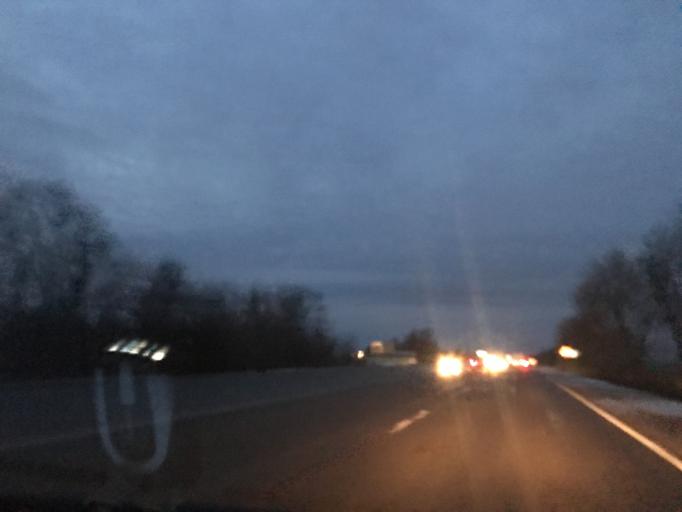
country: RU
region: Rostov
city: Bataysk
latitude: 47.0350
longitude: 39.7408
